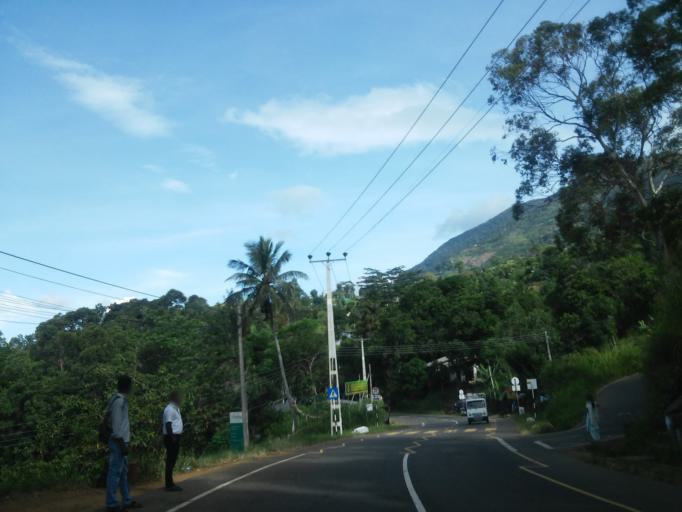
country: LK
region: Uva
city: Haputale
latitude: 6.7639
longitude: 80.9070
